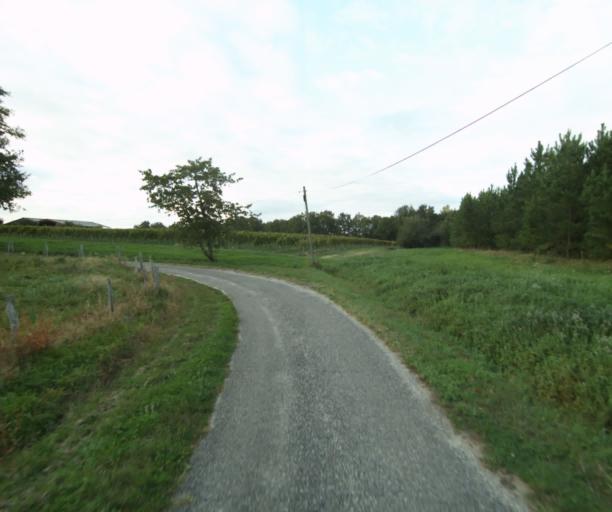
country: FR
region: Aquitaine
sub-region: Departement des Landes
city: Gabarret
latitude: 43.9724
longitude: 0.0822
